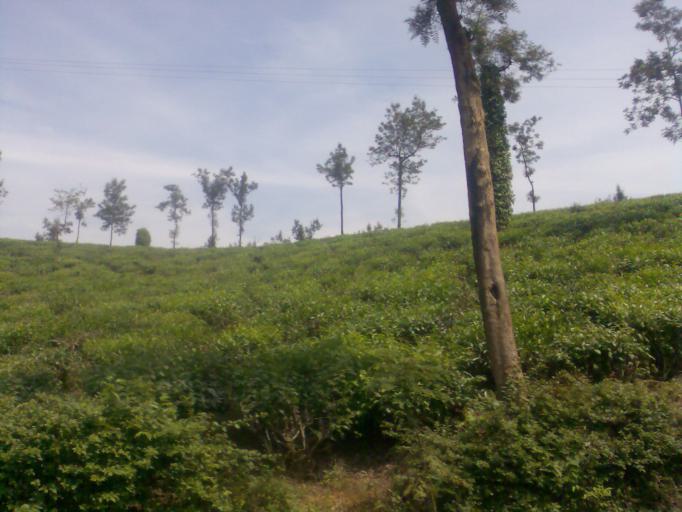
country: IN
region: Kerala
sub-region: Wayanad
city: Kalpetta
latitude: 11.5262
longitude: 76.0235
